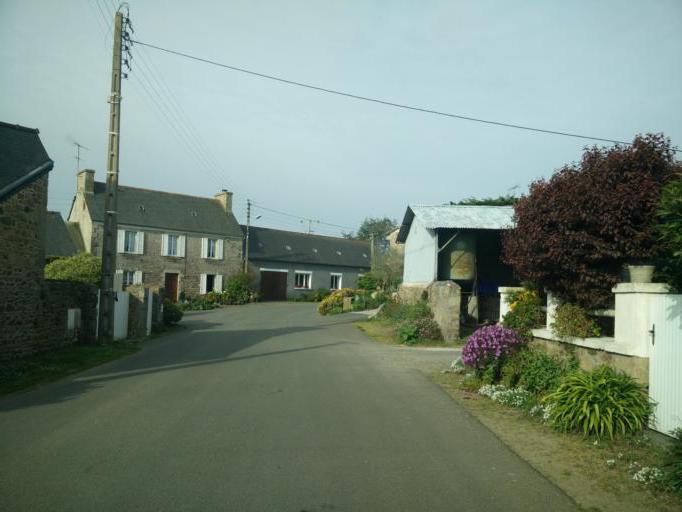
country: FR
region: Brittany
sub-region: Departement des Cotes-d'Armor
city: Lezardrieux
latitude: 48.8268
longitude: -3.0887
